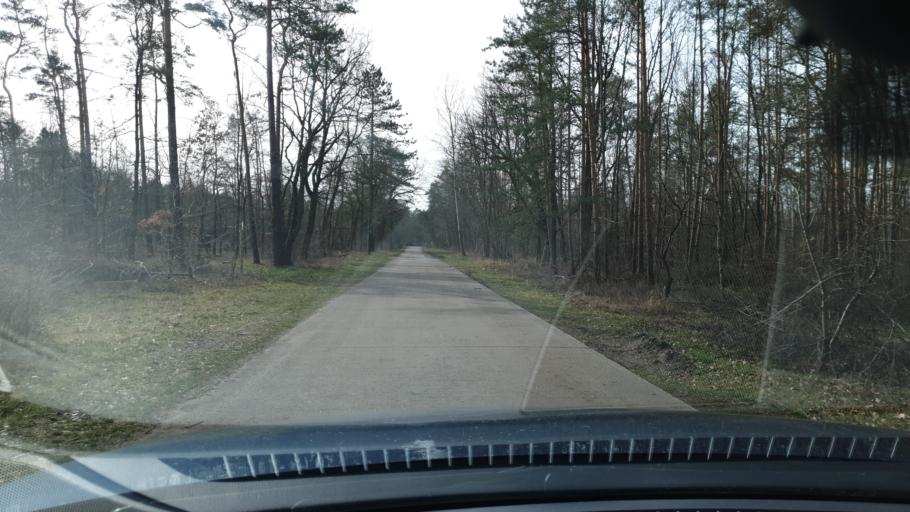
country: DE
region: Saxony-Anhalt
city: Vockerode
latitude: 51.8164
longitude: 12.3363
